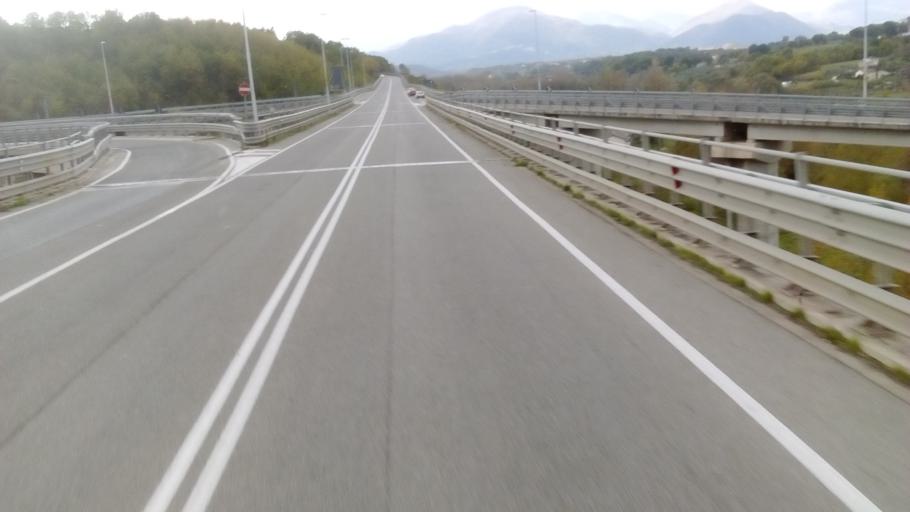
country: IT
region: Molise
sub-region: Provincia di Isernia
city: Isernia
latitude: 41.5795
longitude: 14.2220
